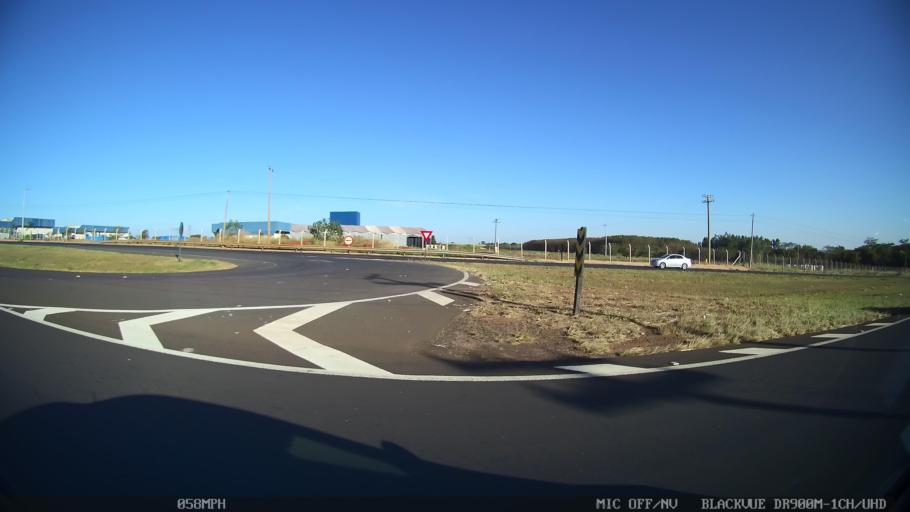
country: BR
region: Sao Paulo
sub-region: Olimpia
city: Olimpia
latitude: -20.7169
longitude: -49.0012
